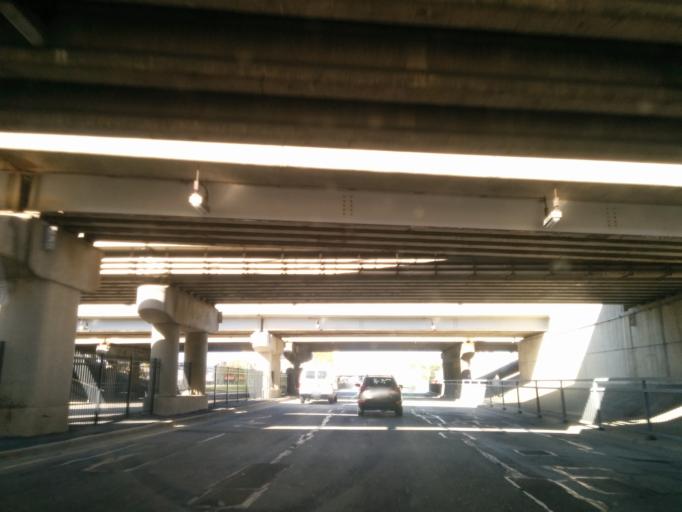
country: US
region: Illinois
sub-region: Cook County
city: Rosemont
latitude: 41.9833
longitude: -87.8614
